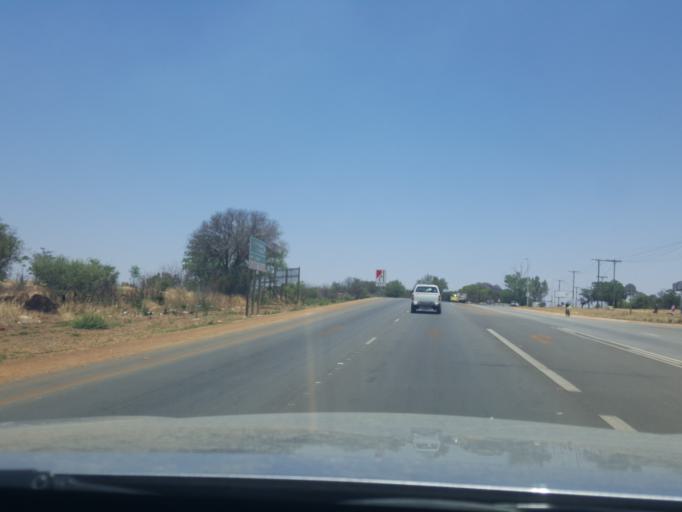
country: ZA
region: North-West
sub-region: Ngaka Modiri Molema District Municipality
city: Zeerust
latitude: -25.5521
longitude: 26.0717
